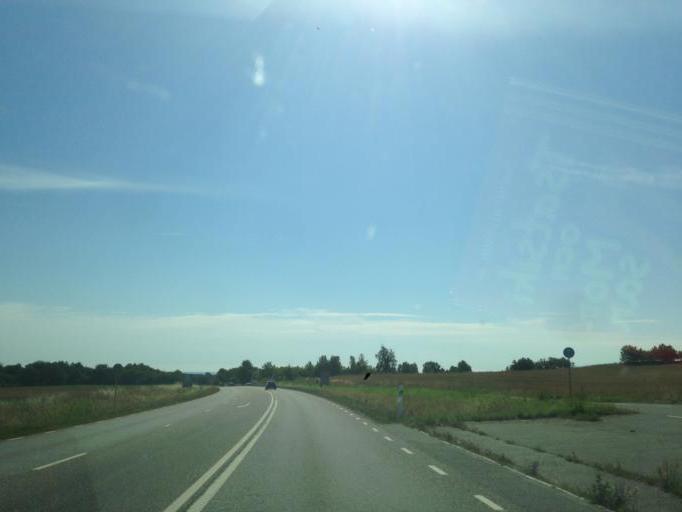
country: SE
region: Skane
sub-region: Simrishamns Kommun
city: Kivik
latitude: 55.6375
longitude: 14.2330
